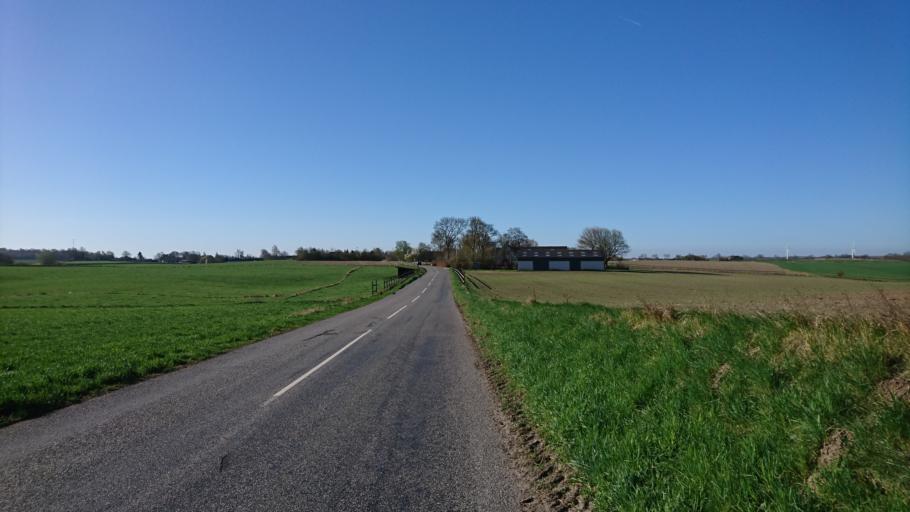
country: DK
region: Capital Region
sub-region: Frederikssund Kommune
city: Skibby
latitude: 55.7320
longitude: 11.9286
